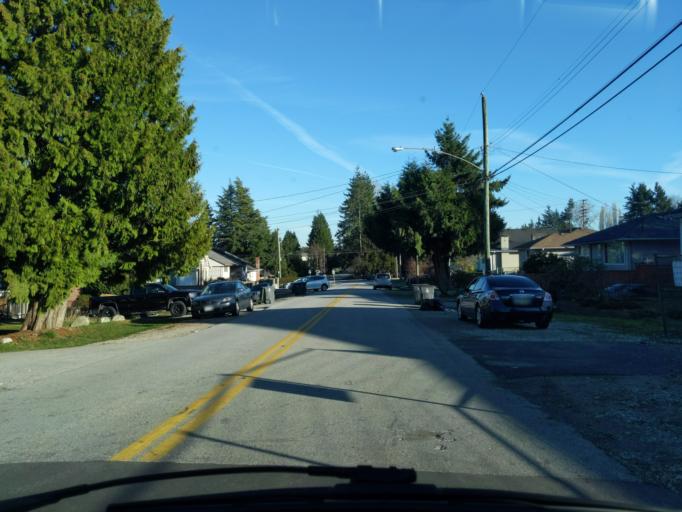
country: CA
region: British Columbia
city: New Westminster
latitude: 49.1962
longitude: -122.8581
